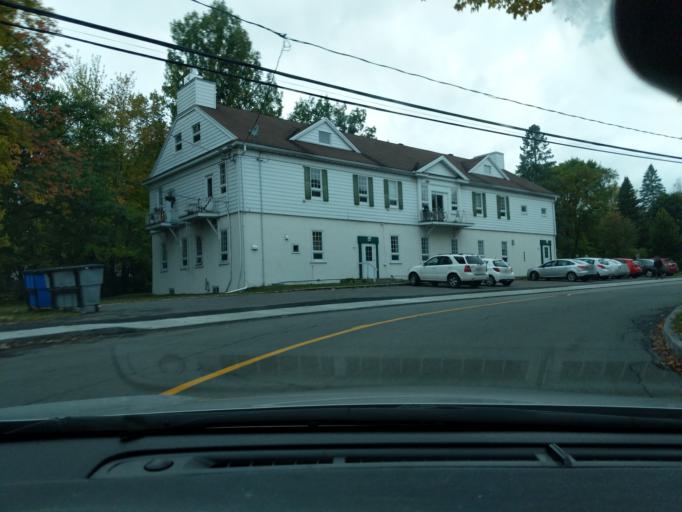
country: CA
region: Quebec
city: Quebec
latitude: 46.7665
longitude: -71.2667
